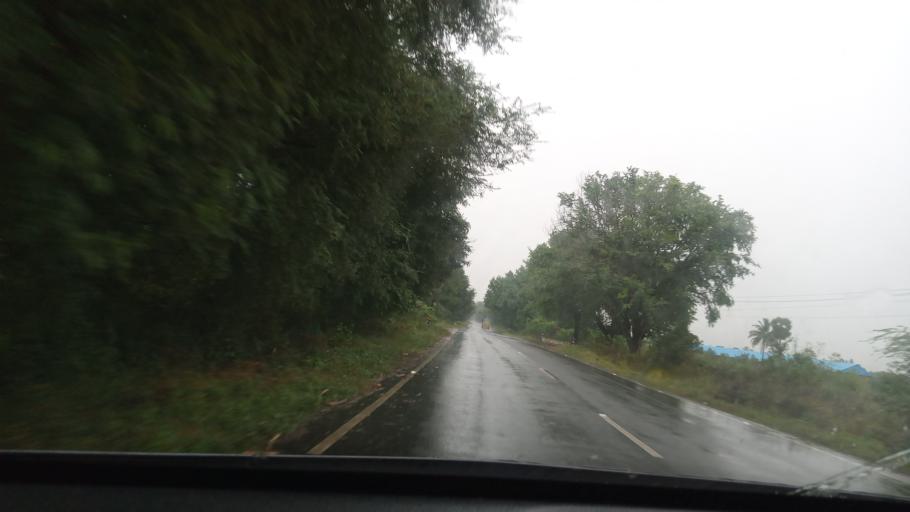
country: IN
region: Tamil Nadu
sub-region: Vellore
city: Kalavai
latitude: 12.8409
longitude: 79.4027
